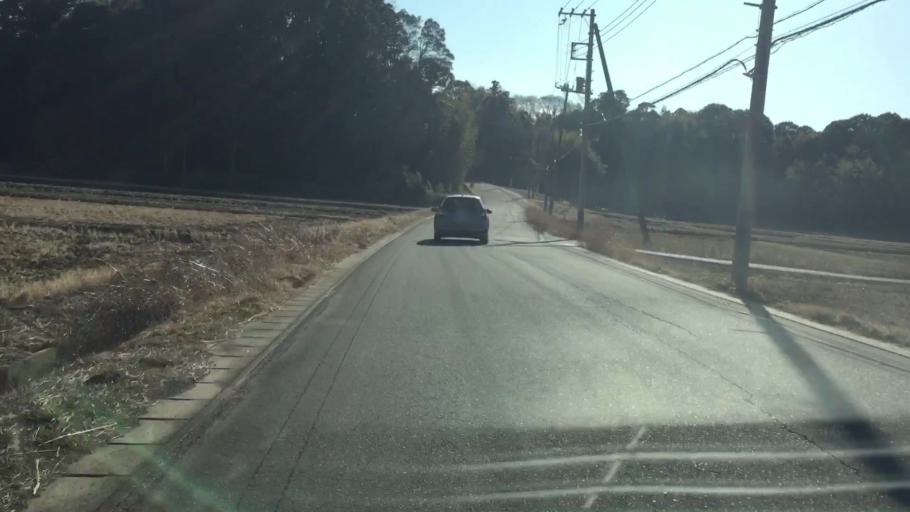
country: JP
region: Chiba
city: Shiroi
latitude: 35.8219
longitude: 140.1204
